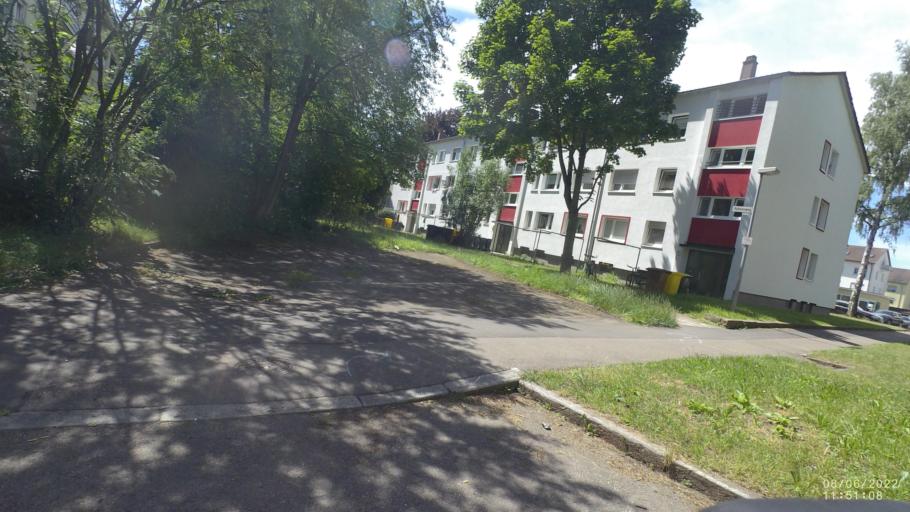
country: DE
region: Baden-Wuerttemberg
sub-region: Regierungsbezirk Stuttgart
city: Fellbach
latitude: 48.8199
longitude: 9.2808
